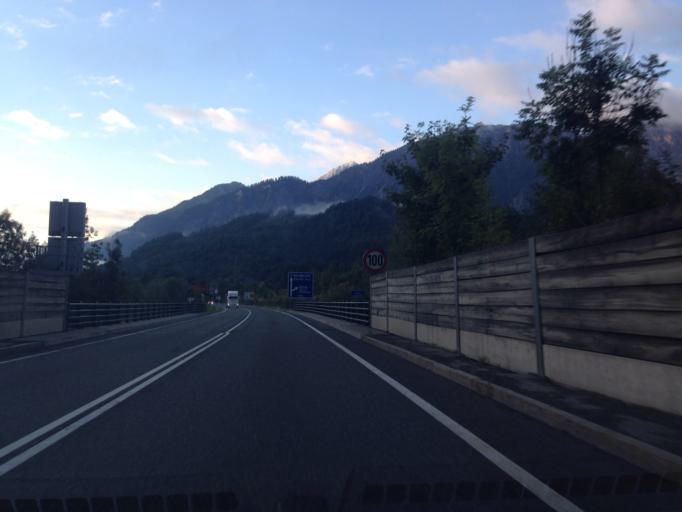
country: AT
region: Tyrol
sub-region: Politischer Bezirk Reutte
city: Vils
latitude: 47.5548
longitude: 10.6562
